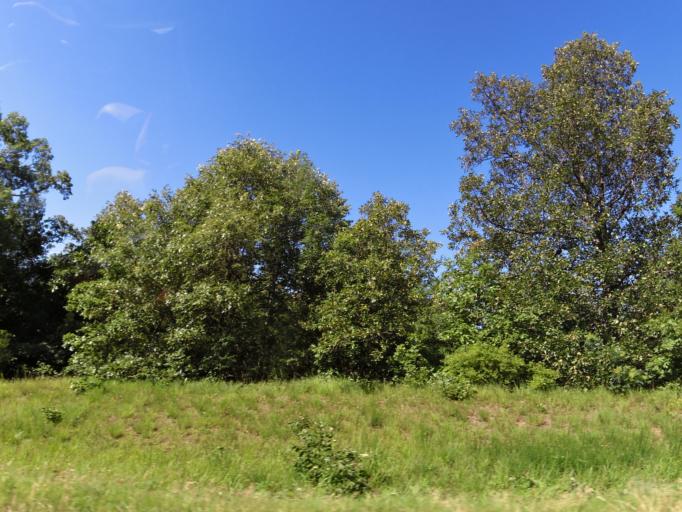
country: US
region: Arkansas
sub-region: Clay County
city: Piggott
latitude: 36.4096
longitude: -90.2202
